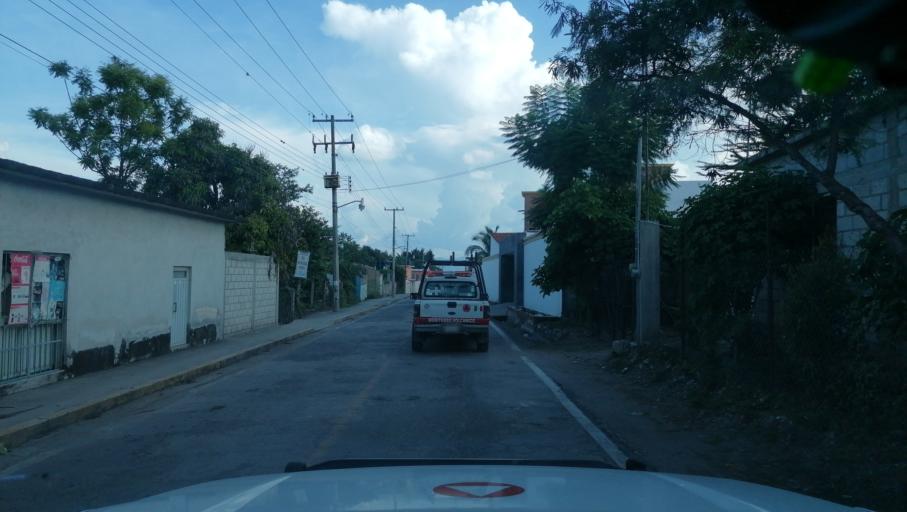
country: MX
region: Morelos
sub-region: Ayala
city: Abelardo L. Rodriguez
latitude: 18.7220
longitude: -98.9924
